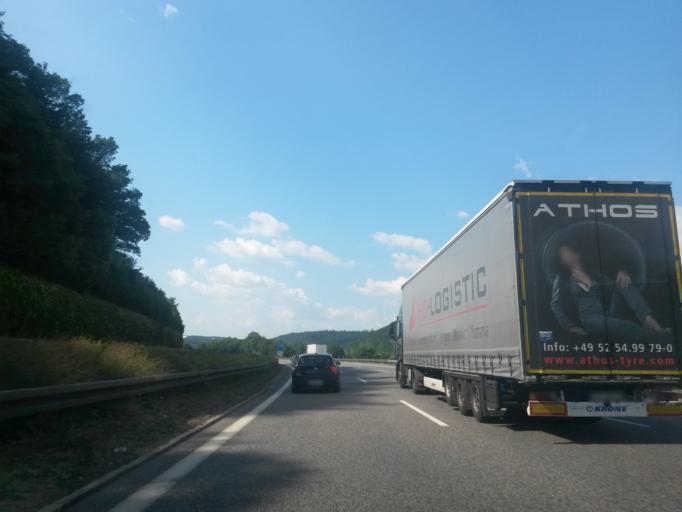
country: DE
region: Bavaria
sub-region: Regierungsbezirk Mittelfranken
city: Greding
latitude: 49.0238
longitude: 11.3677
